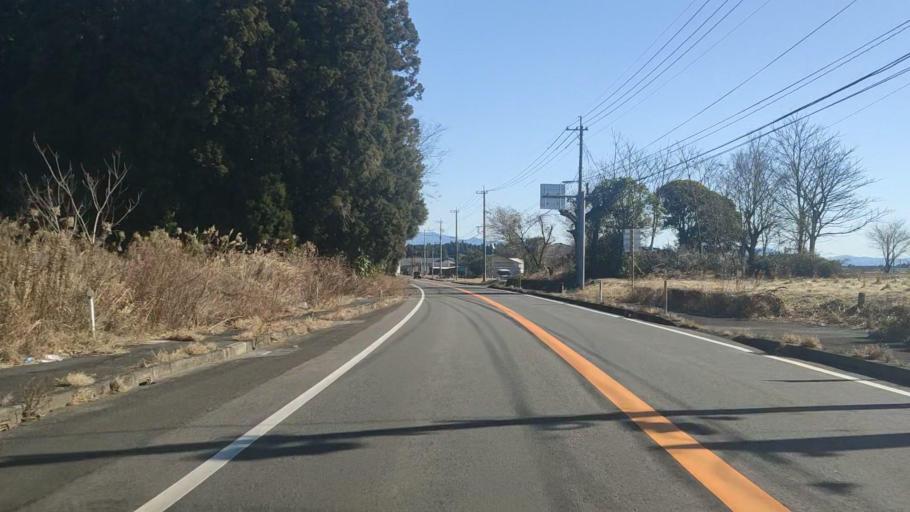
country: JP
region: Kagoshima
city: Sueyoshicho-ninokata
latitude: 31.6944
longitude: 130.9814
